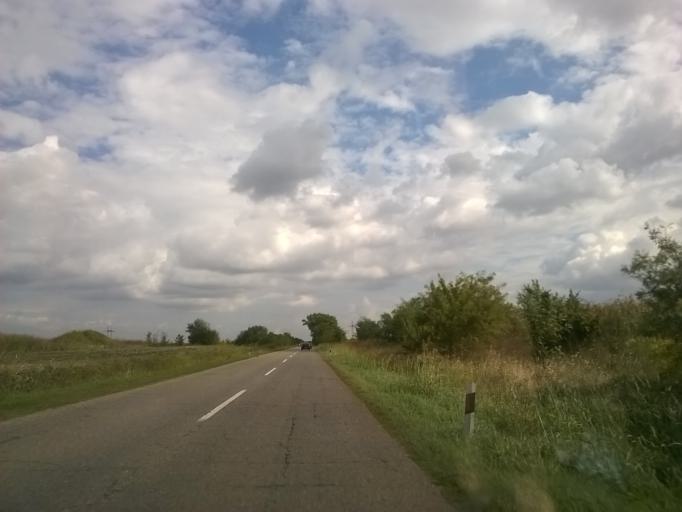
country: RS
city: Padina
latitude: 45.1169
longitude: 20.6827
